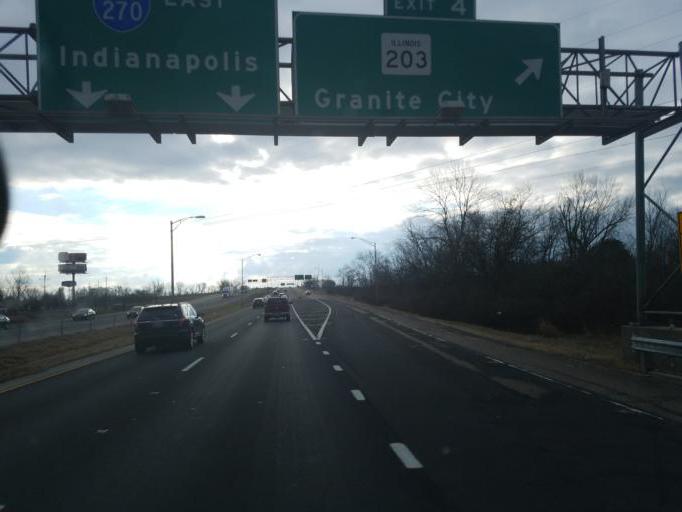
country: US
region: Illinois
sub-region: Madison County
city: Mitchell
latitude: 38.7621
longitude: -90.1017
